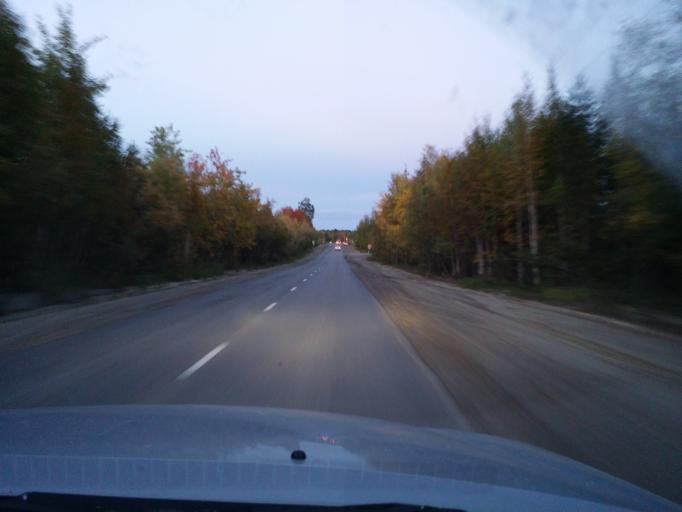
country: RU
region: Khanty-Mansiyskiy Avtonomnyy Okrug
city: Nizhnevartovsk
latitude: 60.9923
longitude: 76.4240
